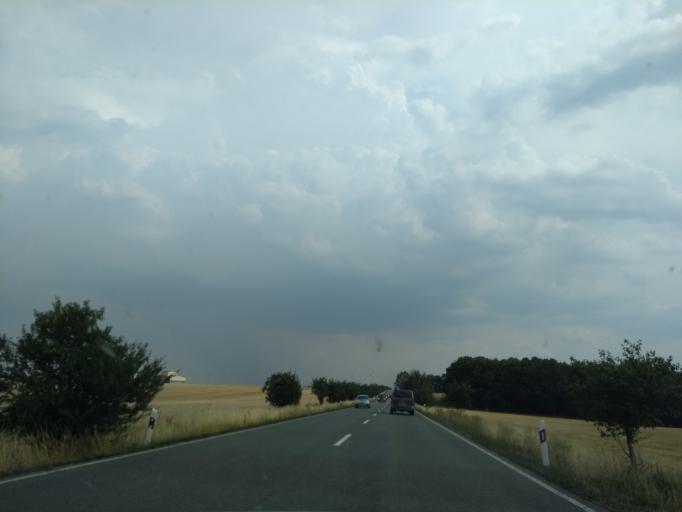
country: DE
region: Saxony-Anhalt
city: Zeitz
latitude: 50.9950
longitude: 12.1352
